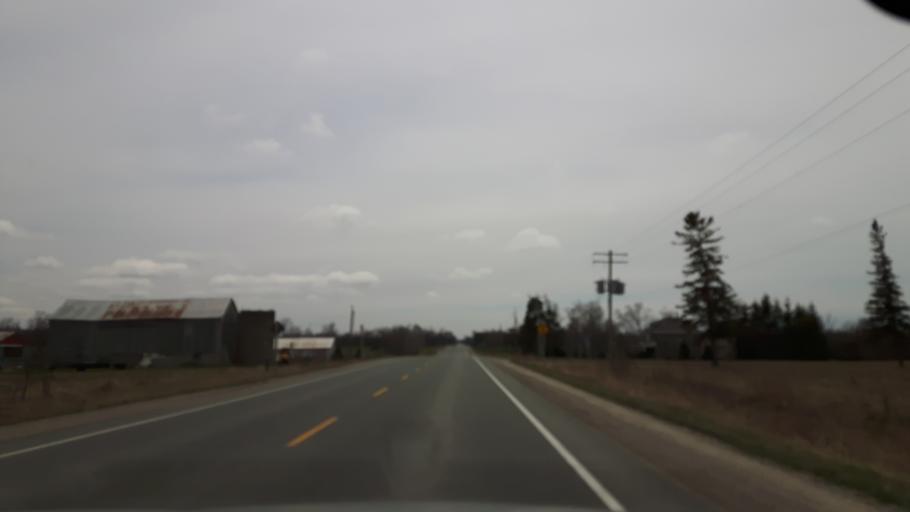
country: CA
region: Ontario
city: Goderich
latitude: 43.6083
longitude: -81.7057
